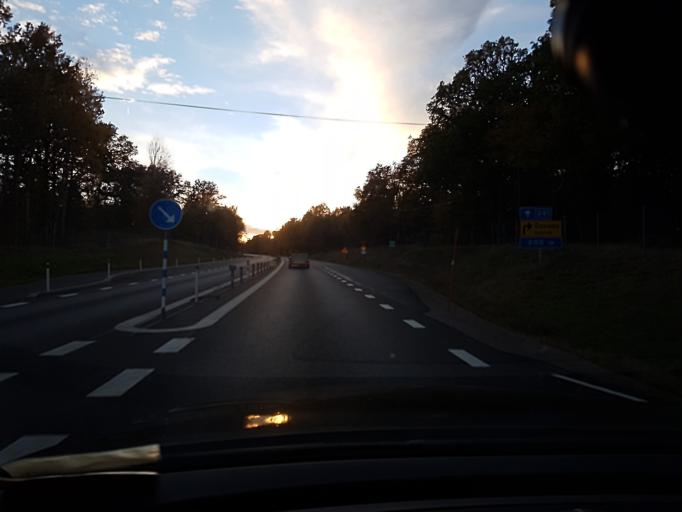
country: SE
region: Kronoberg
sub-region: Ljungby Kommun
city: Ljungby
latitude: 56.7605
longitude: 13.7740
